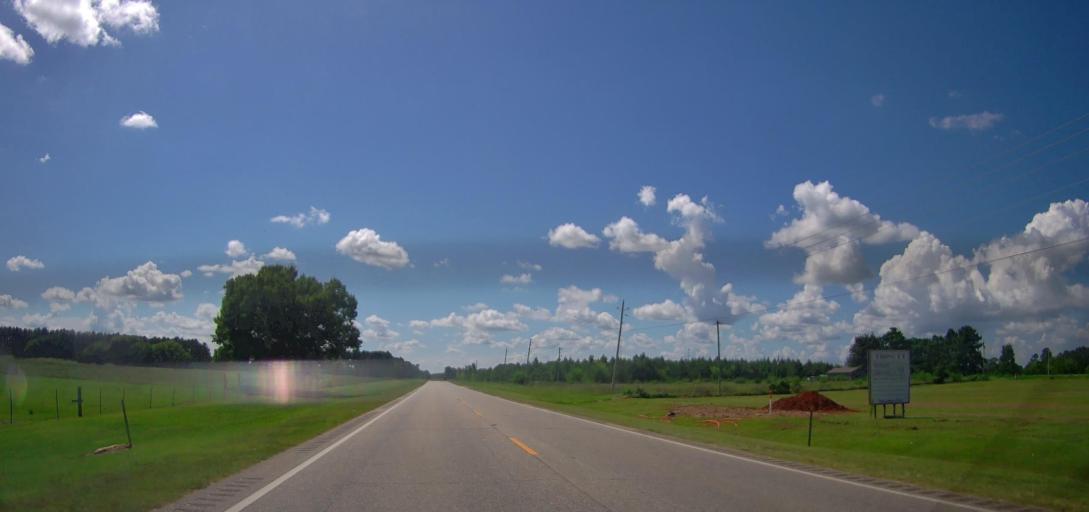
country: US
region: Alabama
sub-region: Elmore County
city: Tallassee
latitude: 32.3876
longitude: -85.8880
